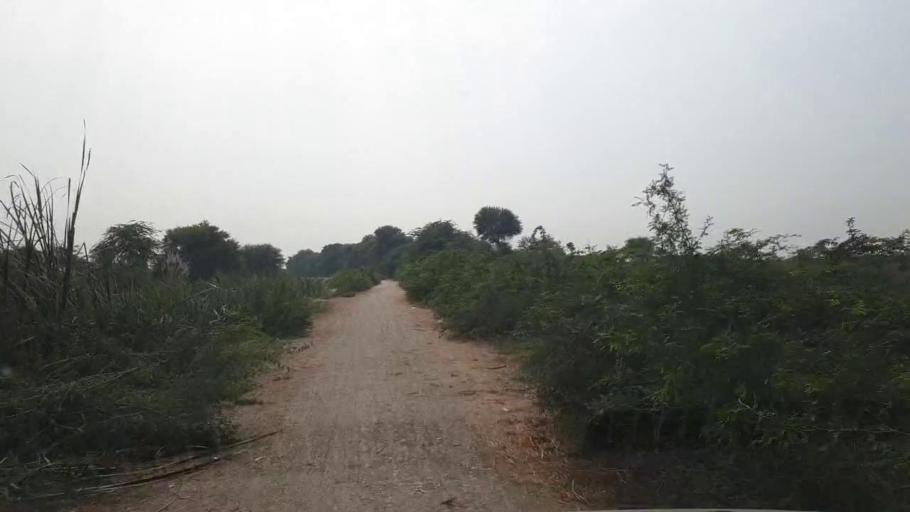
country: PK
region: Sindh
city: Matli
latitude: 25.0088
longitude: 68.7016
